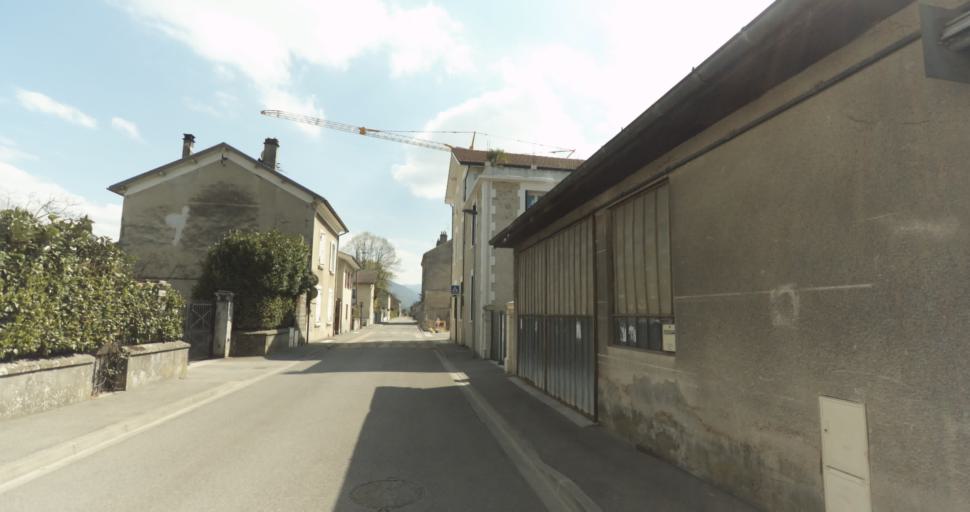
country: FR
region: Rhone-Alpes
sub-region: Departement de l'Isere
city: Saint-Marcellin
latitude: 45.1505
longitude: 5.3246
